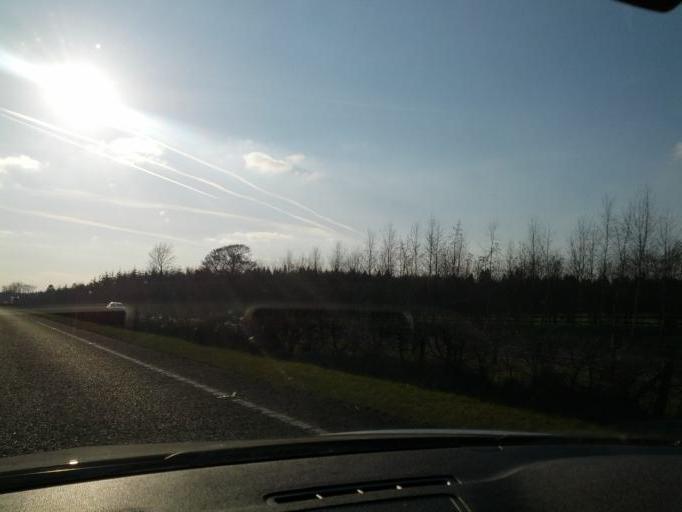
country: IE
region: Leinster
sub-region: Laois
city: Portarlington
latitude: 53.1039
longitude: -7.1418
